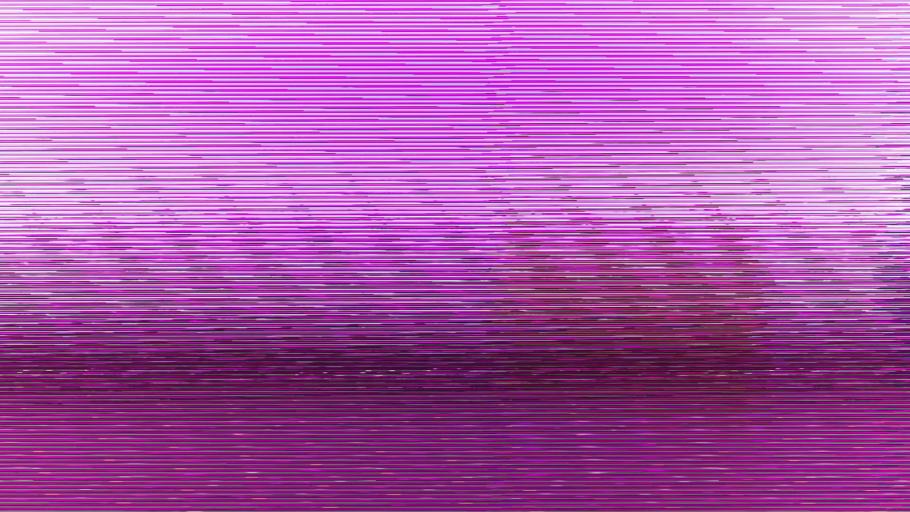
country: US
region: Michigan
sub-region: Washtenaw County
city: Ypsilanti
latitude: 42.2279
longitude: -83.6208
